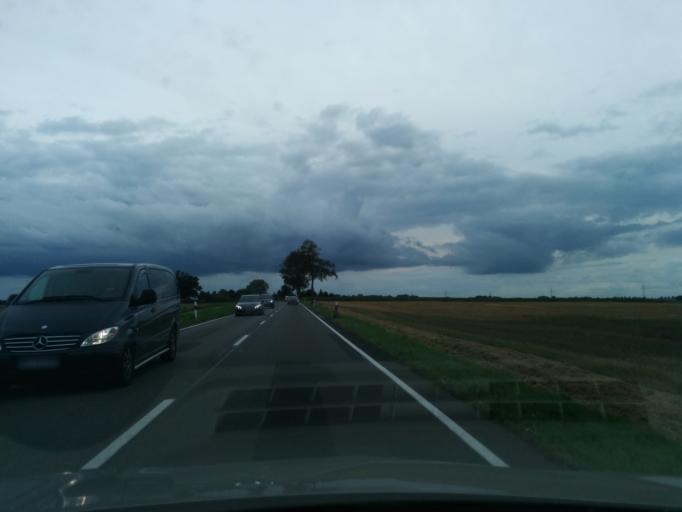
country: DE
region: Mecklenburg-Vorpommern
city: Zussow
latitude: 53.9926
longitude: 13.5806
